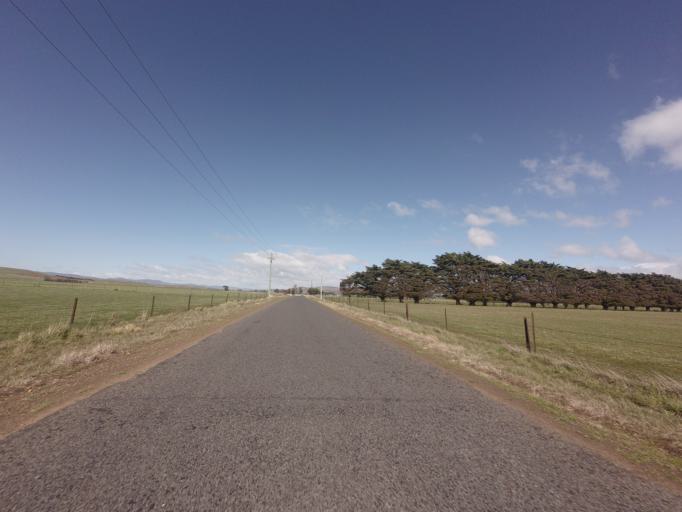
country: AU
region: Tasmania
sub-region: Northern Midlands
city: Evandale
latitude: -41.9932
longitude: 147.4534
